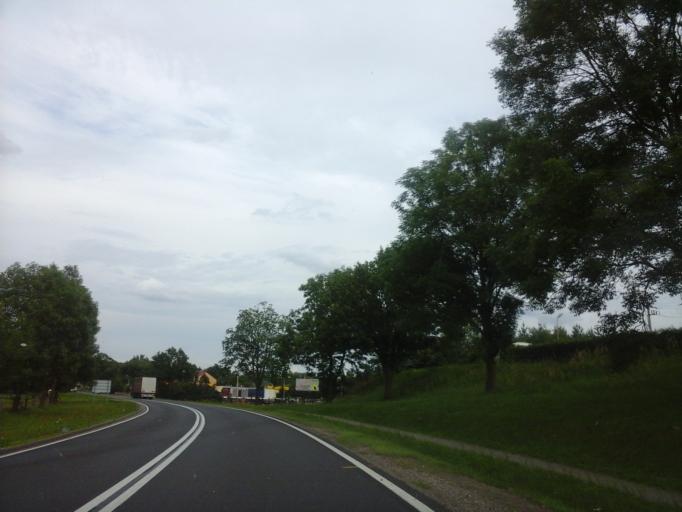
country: PL
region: West Pomeranian Voivodeship
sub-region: Powiat stargardzki
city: Suchan
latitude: 53.2770
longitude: 15.3343
